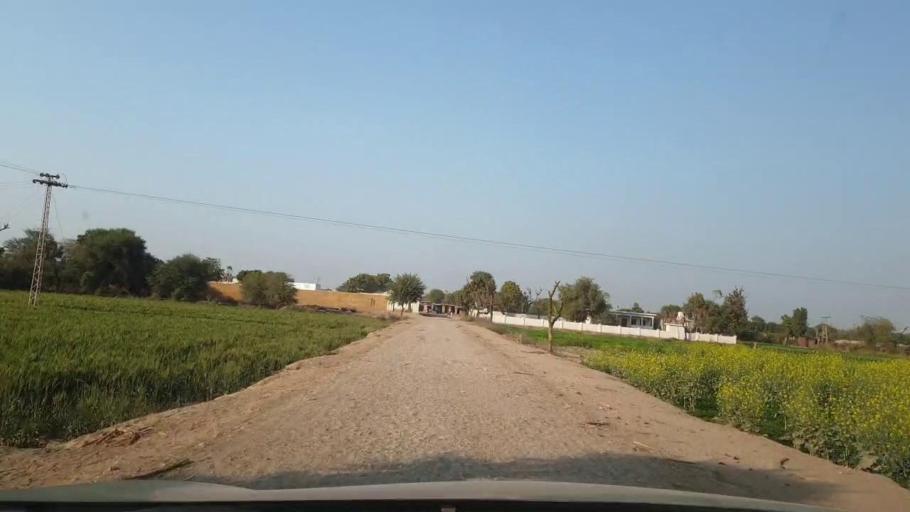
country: PK
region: Sindh
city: Tando Allahyar
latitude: 25.5820
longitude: 68.7802
